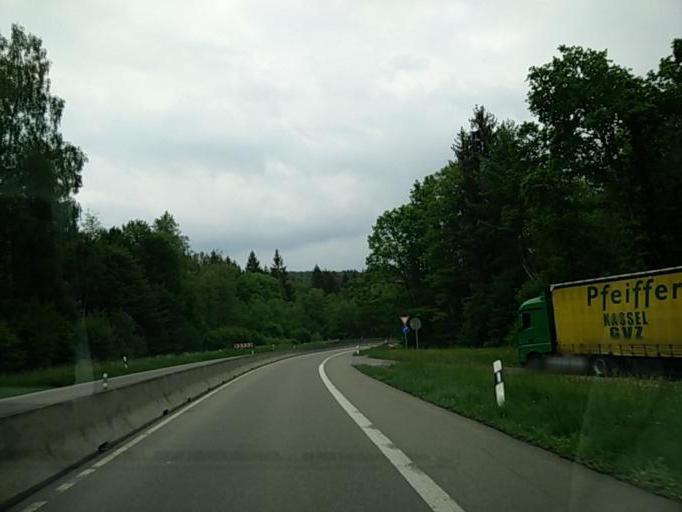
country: DE
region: Baden-Wuerttemberg
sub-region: Regierungsbezirk Stuttgart
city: Weil im Schonbuch
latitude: 48.5855
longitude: 9.0657
